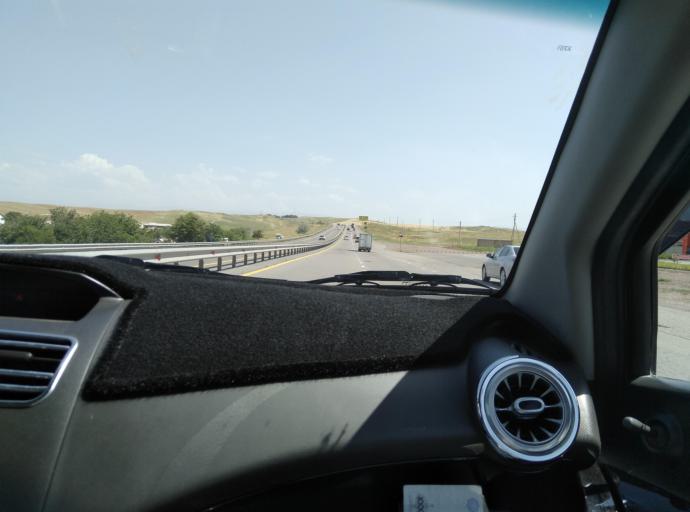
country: UZ
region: Toshkent
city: Ohangaron
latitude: 40.9761
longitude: 69.5441
